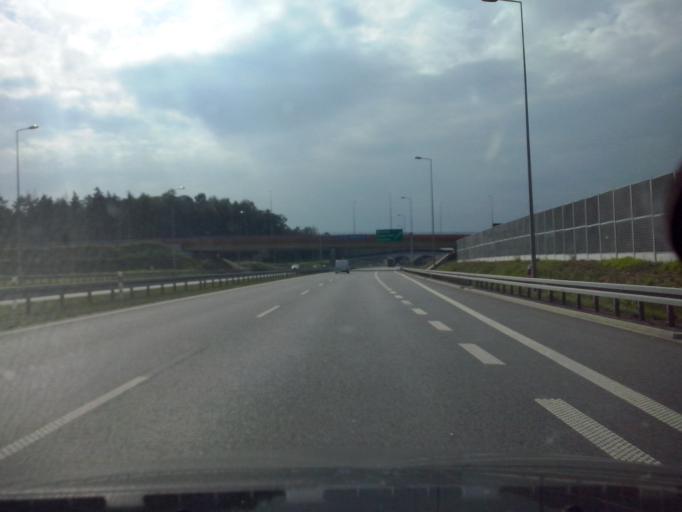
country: PL
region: Lesser Poland Voivodeship
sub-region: Powiat brzeski
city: Jasien
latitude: 49.9925
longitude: 20.5893
